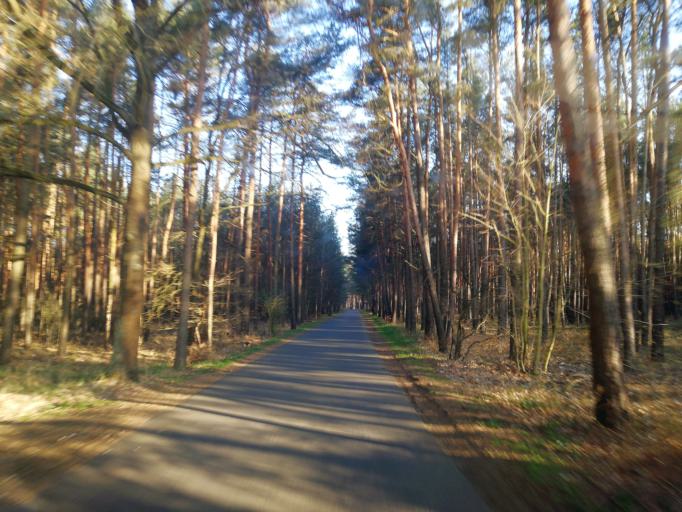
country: DE
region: Brandenburg
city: Drahnsdorf
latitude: 51.8898
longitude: 13.5796
